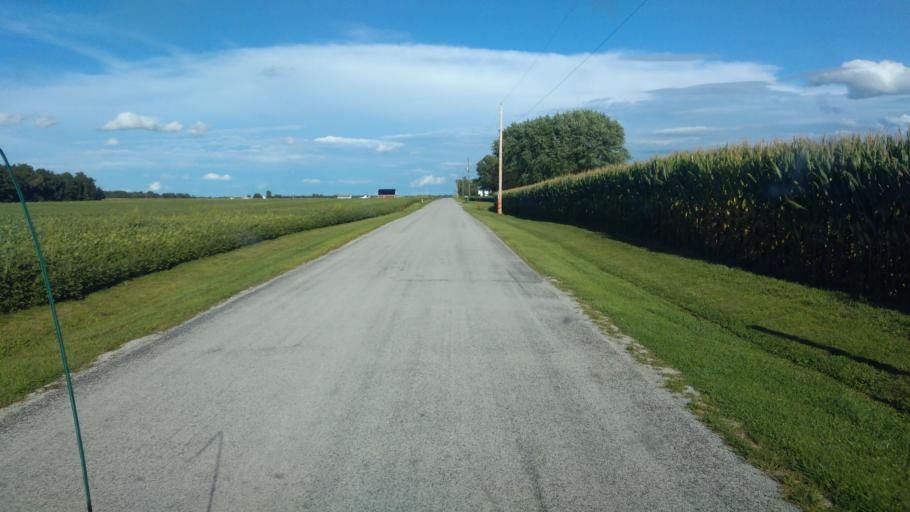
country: US
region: Ohio
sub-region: Hardin County
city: Kenton
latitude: 40.7613
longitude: -83.6666
